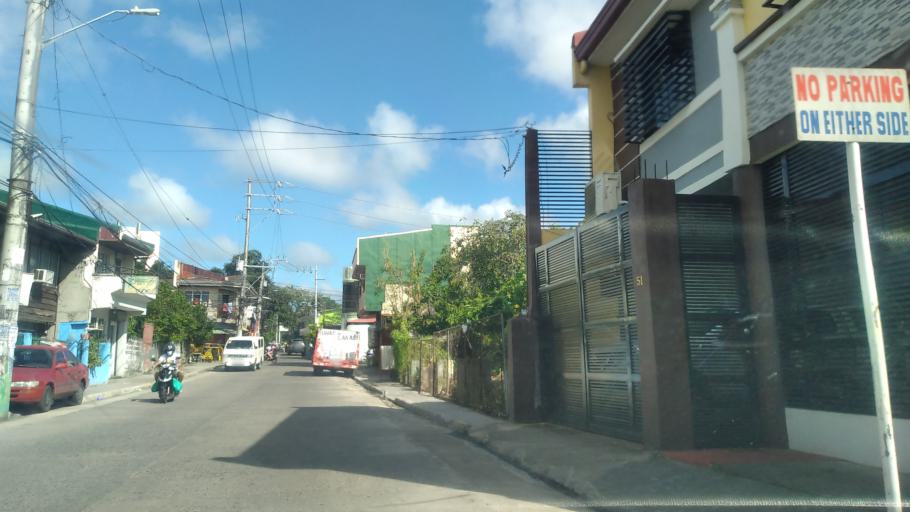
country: PH
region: Calabarzon
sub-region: Province of Quezon
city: Lucena
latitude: 13.9393
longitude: 121.6119
